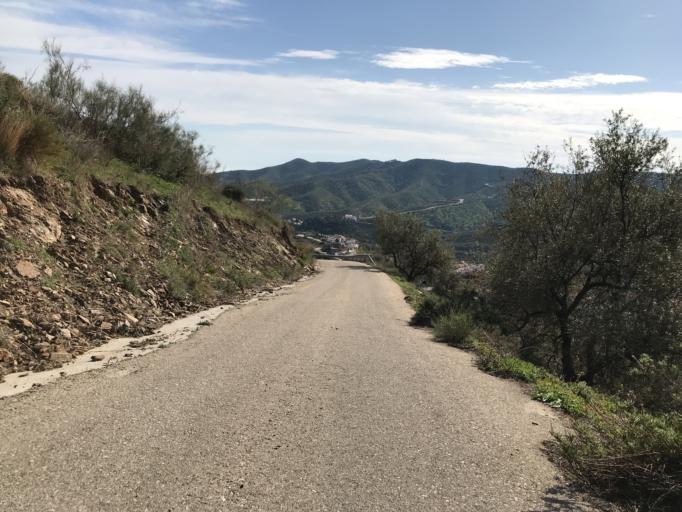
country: ES
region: Andalusia
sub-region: Provincia de Malaga
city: Valdes
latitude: 36.7731
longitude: -4.2151
